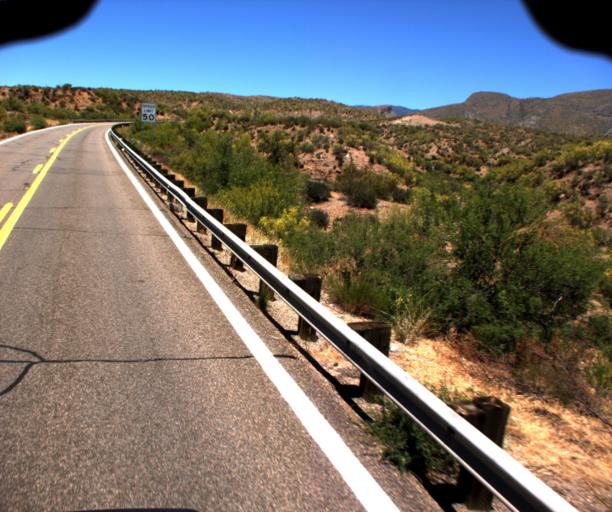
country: US
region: Arizona
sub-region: Pinal County
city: Kearny
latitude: 33.1521
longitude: -110.8045
